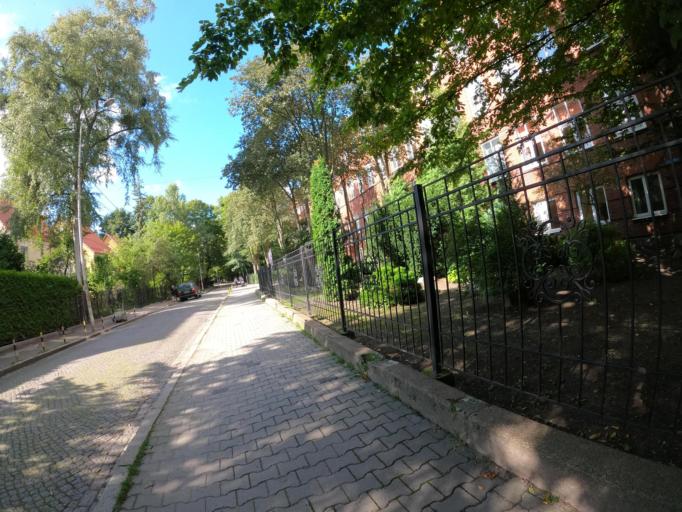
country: RU
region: Kaliningrad
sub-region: Gorod Kaliningrad
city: Kaliningrad
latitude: 54.7289
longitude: 20.4694
